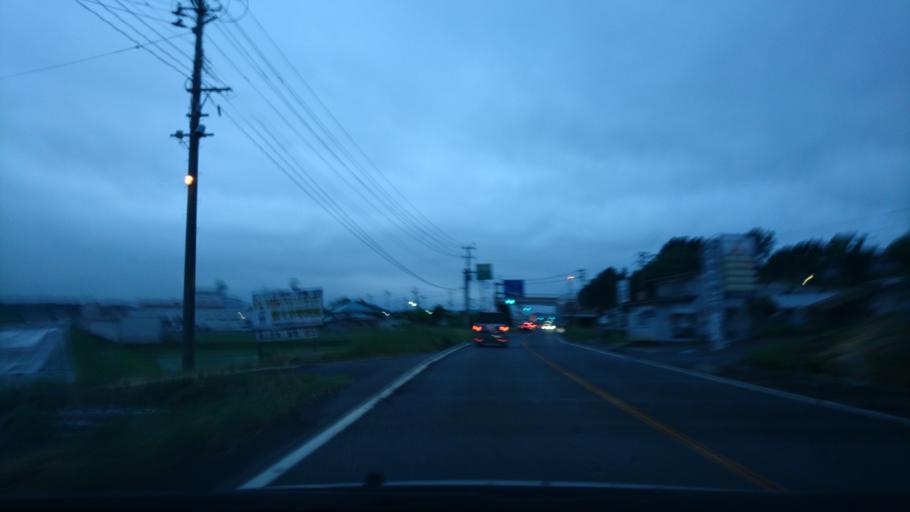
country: JP
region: Iwate
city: Ichinoseki
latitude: 38.8064
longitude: 141.0732
